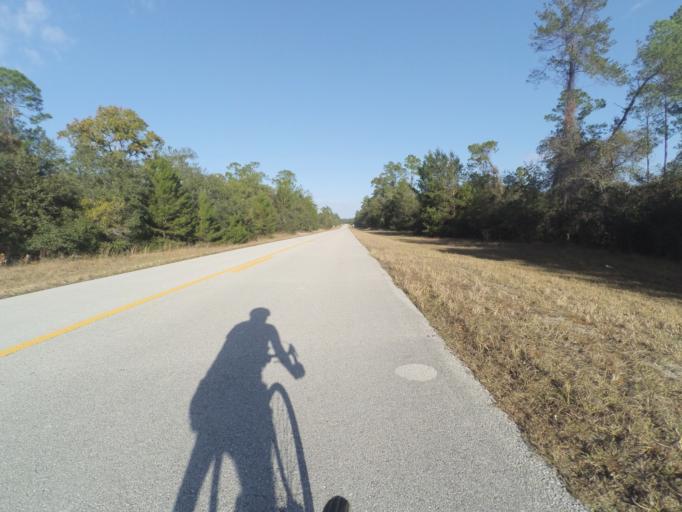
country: US
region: Florida
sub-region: Lake County
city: Astor
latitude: 29.1024
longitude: -81.5663
